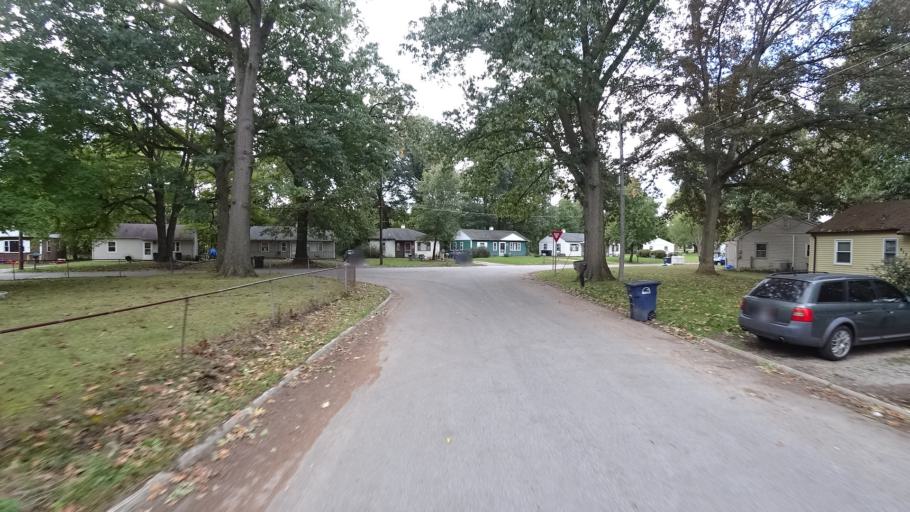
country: US
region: Indiana
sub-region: LaPorte County
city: Trail Creek
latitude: 41.7035
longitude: -86.8677
